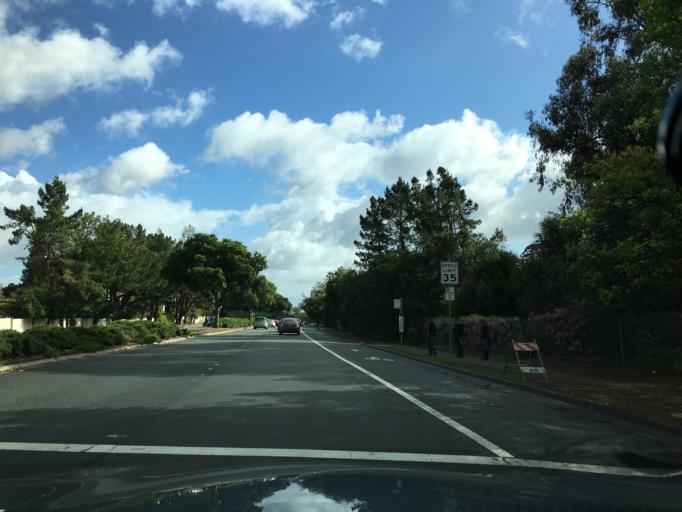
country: US
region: California
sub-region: San Mateo County
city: West Menlo Park
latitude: 37.4237
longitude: -122.1953
